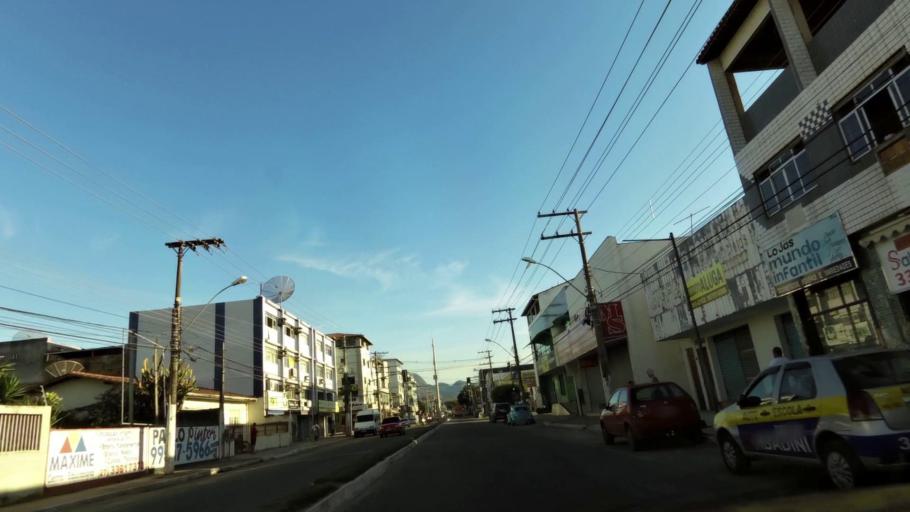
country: BR
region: Espirito Santo
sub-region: Guarapari
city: Guarapari
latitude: -20.6631
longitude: -40.5011
